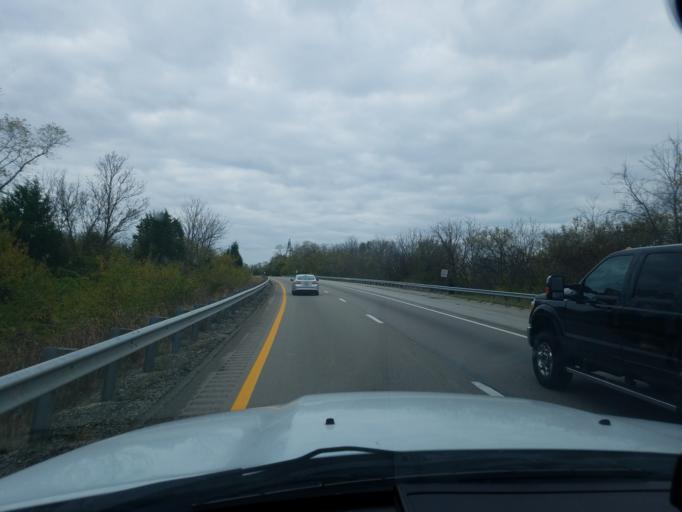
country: US
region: Indiana
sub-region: Switzerland County
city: Vevay
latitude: 38.6748
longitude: -85.0090
